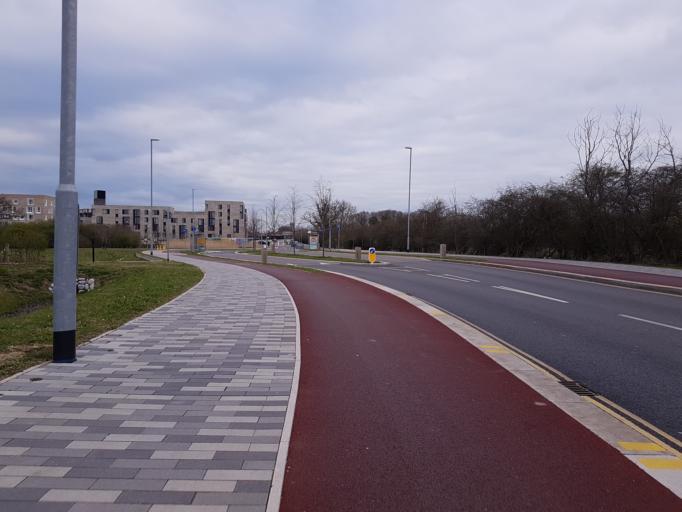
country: GB
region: England
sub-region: Cambridgeshire
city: Girton
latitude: 52.2147
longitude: 0.0858
